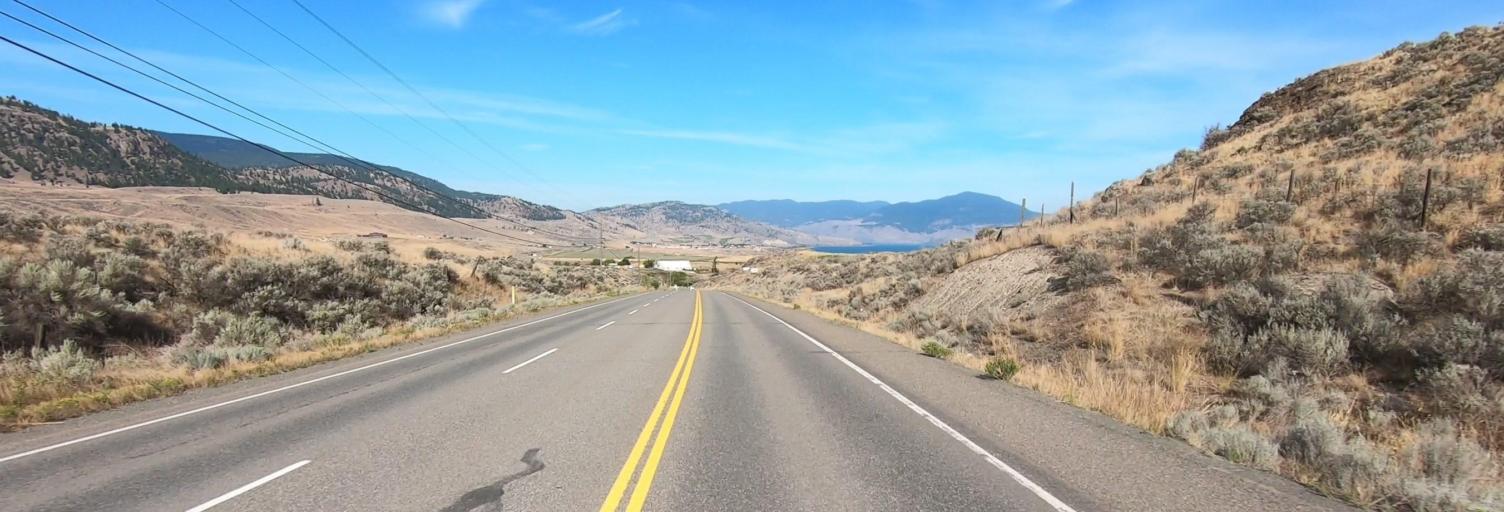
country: CA
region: British Columbia
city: Logan Lake
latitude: 50.7151
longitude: -120.6273
